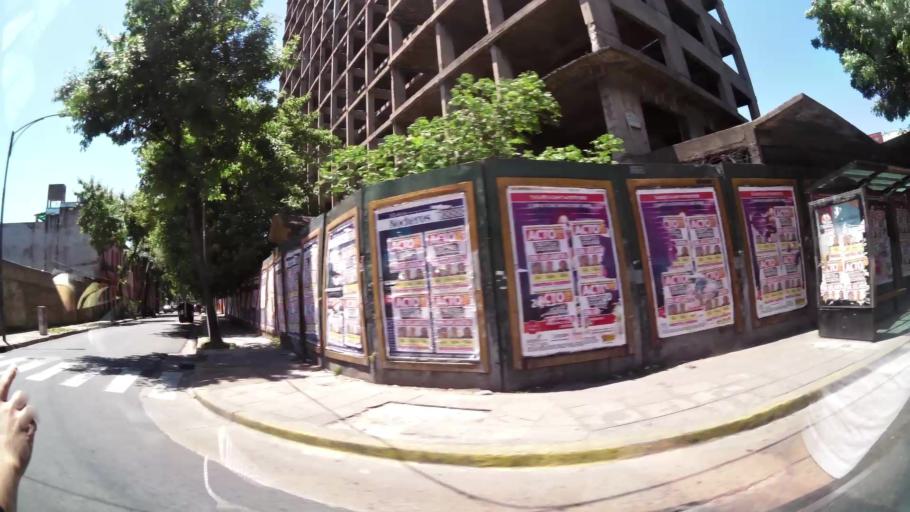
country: AR
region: Buenos Aires
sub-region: Partido de Avellaneda
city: Avellaneda
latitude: -34.6431
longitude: -58.3794
